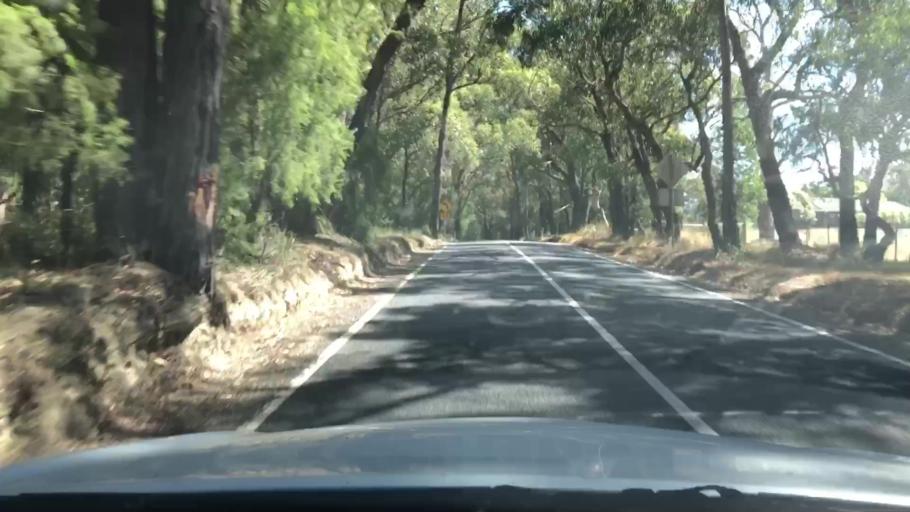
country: AU
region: Victoria
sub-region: Yarra Ranges
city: Macclesfield
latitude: -37.8512
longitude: 145.4868
